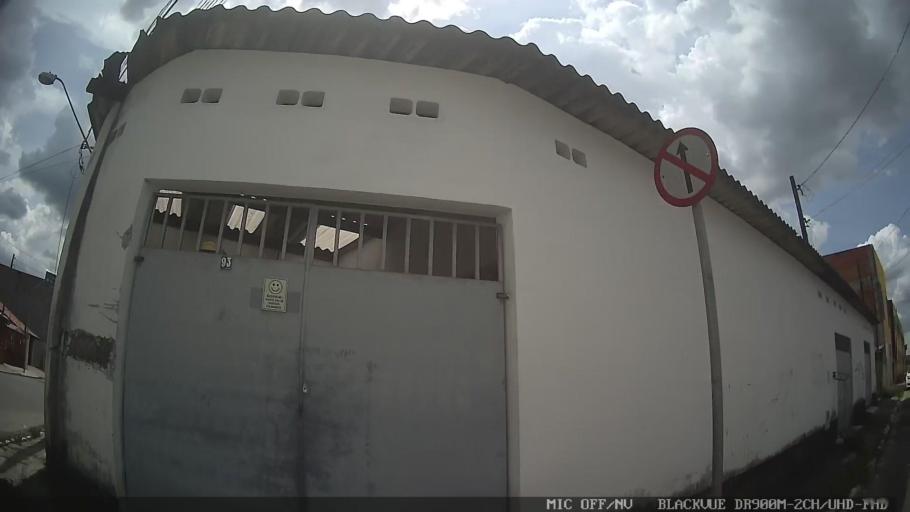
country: BR
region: Sao Paulo
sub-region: Suzano
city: Suzano
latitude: -23.5443
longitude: -46.3057
